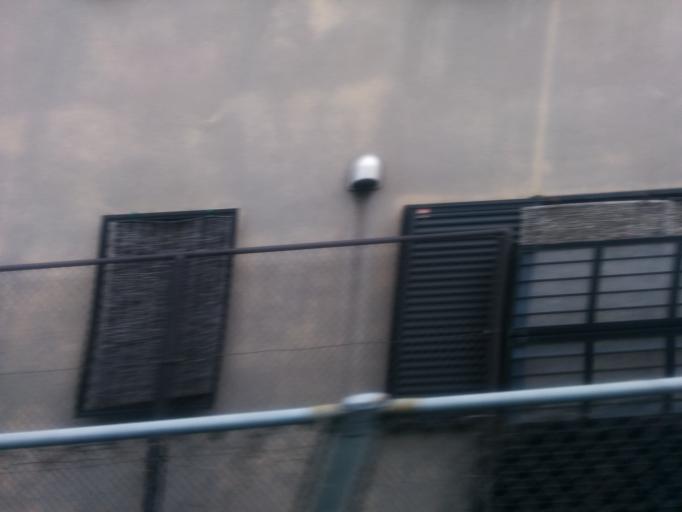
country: JP
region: Kyoto
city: Kyoto
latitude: 34.9630
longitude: 135.7733
